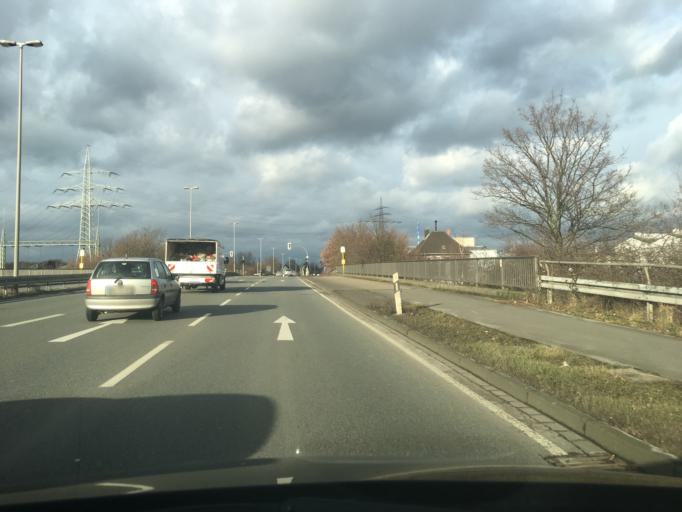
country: DE
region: North Rhine-Westphalia
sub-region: Regierungsbezirk Dusseldorf
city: Oberhausen
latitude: 51.4849
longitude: 6.8409
